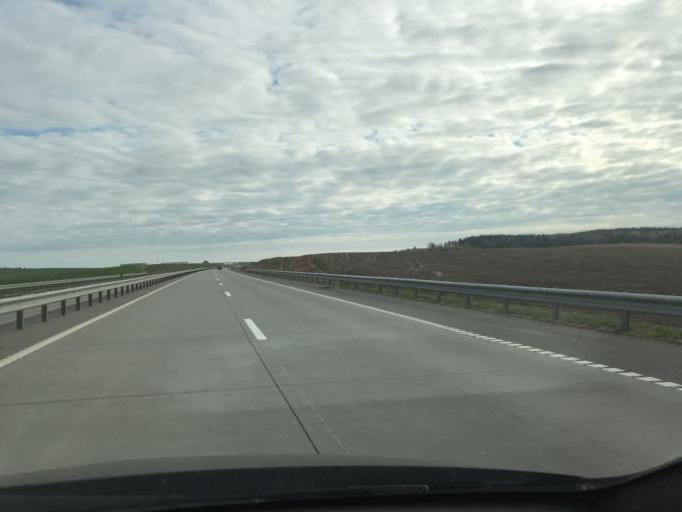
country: BY
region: Minsk
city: Syomkava
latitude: 54.0668
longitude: 27.4784
